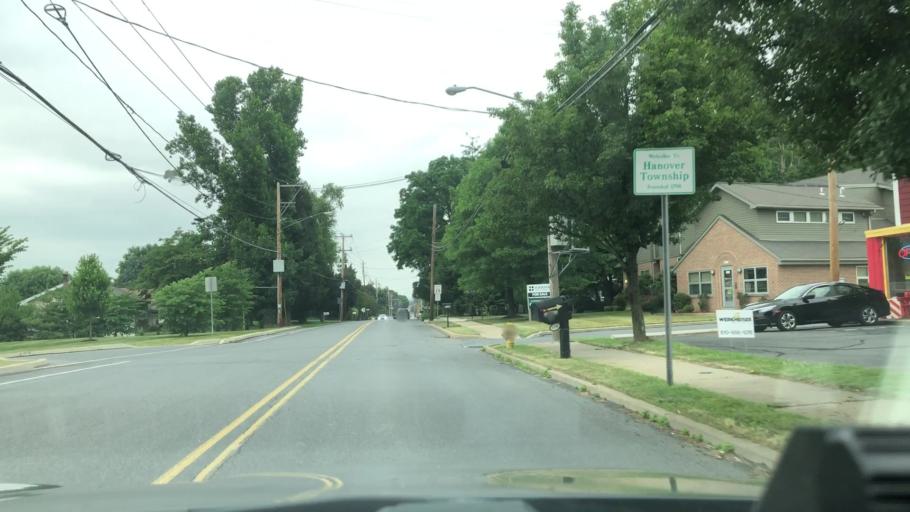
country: US
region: Pennsylvania
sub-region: Northampton County
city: Bethlehem
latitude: 40.6415
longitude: -75.4002
